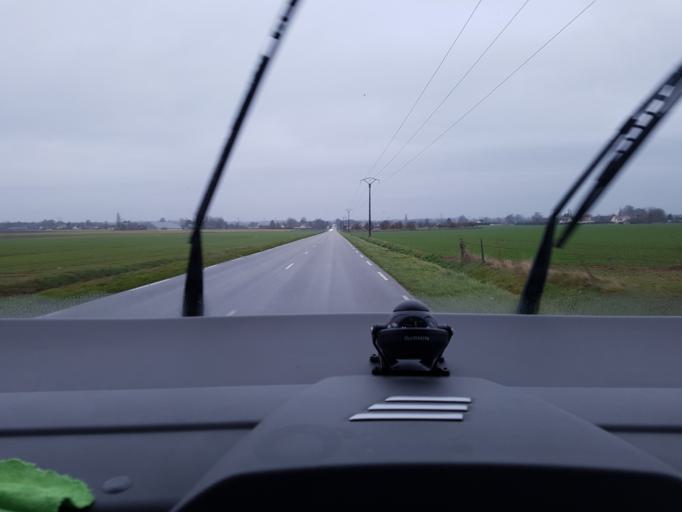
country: FR
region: Haute-Normandie
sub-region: Departement de l'Eure
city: Le Neubourg
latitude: 49.1278
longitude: 0.8725
